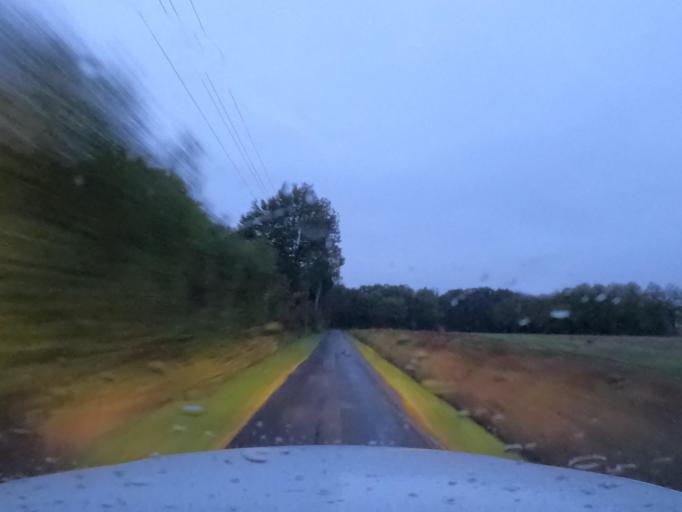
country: DE
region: North Rhine-Westphalia
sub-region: Regierungsbezirk Dusseldorf
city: Hunxe
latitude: 51.6436
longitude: 6.7902
